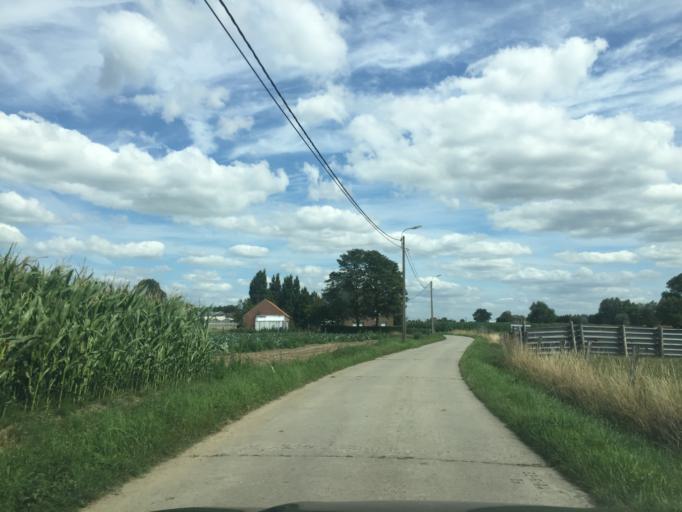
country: BE
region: Flanders
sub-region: Provincie West-Vlaanderen
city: Staden
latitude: 50.9866
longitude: 3.0468
